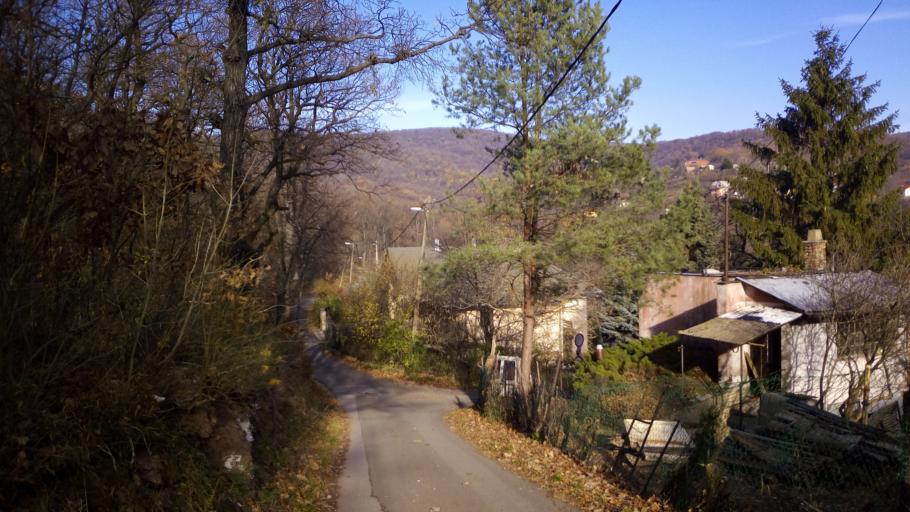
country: HU
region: Baranya
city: Pecs
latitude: 46.0950
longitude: 18.1814
